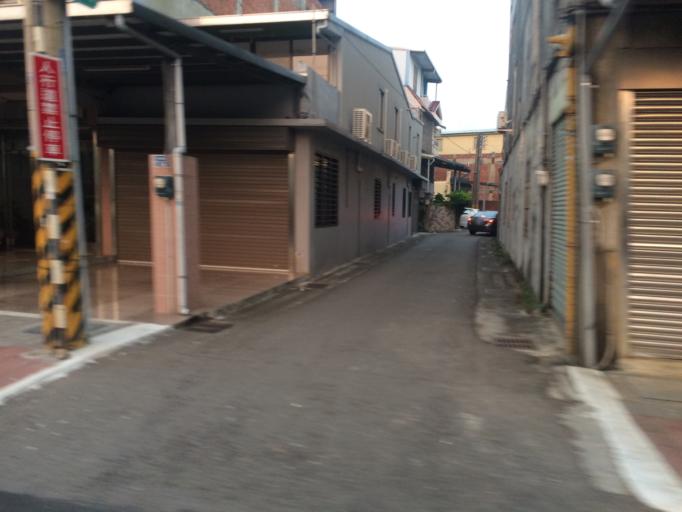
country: TW
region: Taiwan
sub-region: Hsinchu
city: Hsinchu
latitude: 24.7072
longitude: 120.9254
